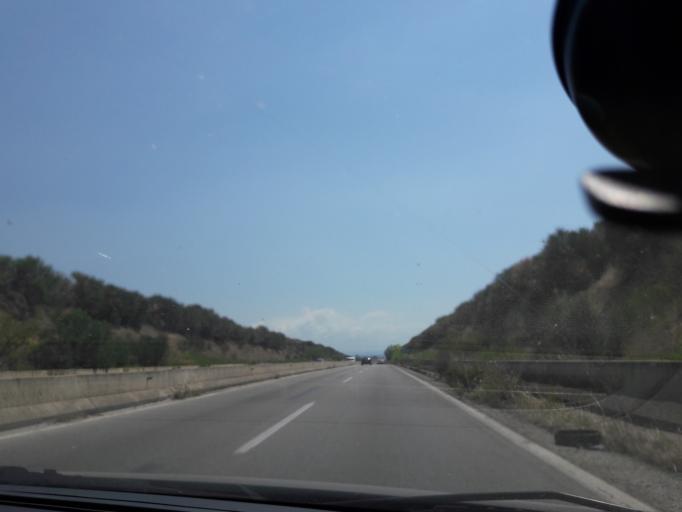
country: GR
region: Central Macedonia
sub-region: Nomos Chalkidikis
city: Nea Triglia
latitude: 40.2965
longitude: 23.1388
